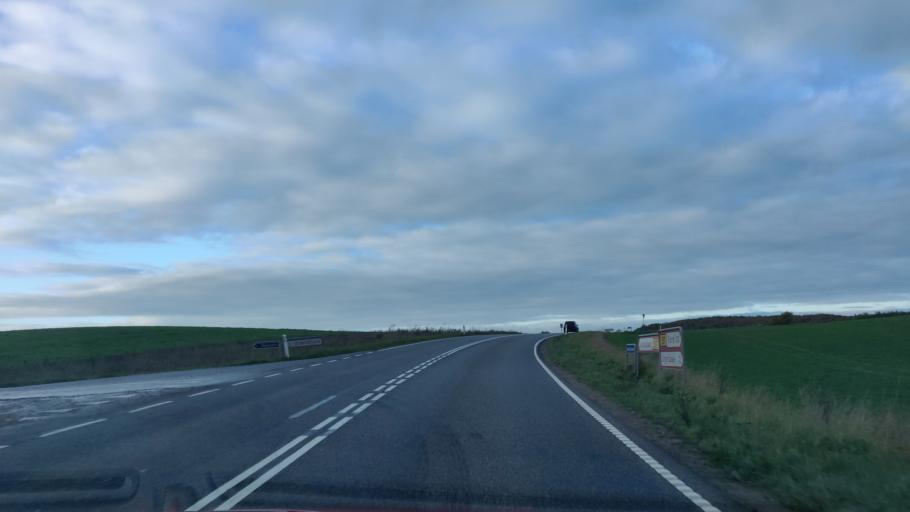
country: DK
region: Zealand
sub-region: Soro Kommune
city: Stenlille
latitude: 55.5993
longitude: 11.6570
